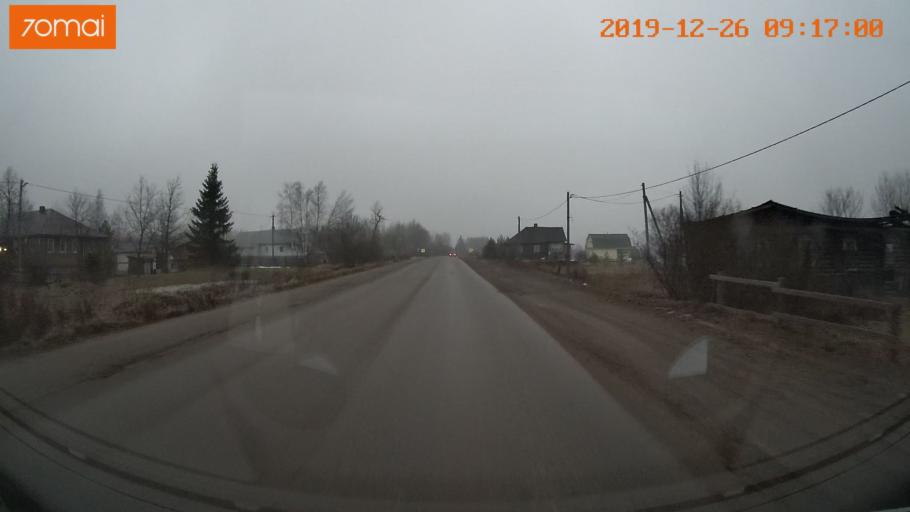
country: RU
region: Vologda
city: Gryazovets
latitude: 58.9250
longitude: 40.2391
